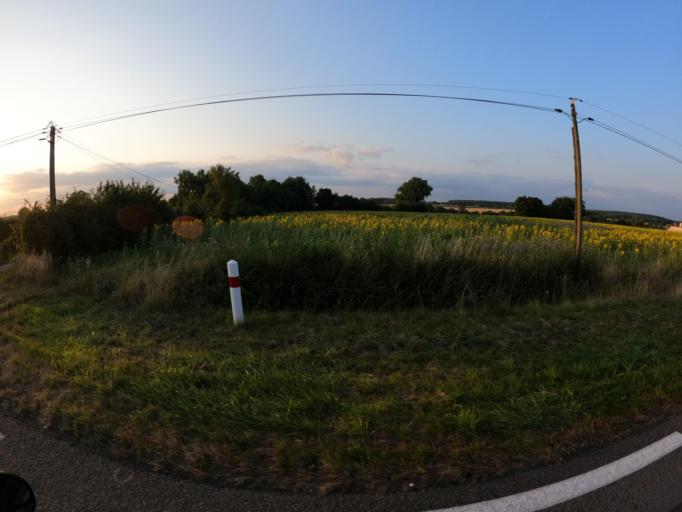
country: FR
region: Pays de la Loire
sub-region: Departement de Maine-et-Loire
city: Mire
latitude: 47.8704
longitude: -0.4728
